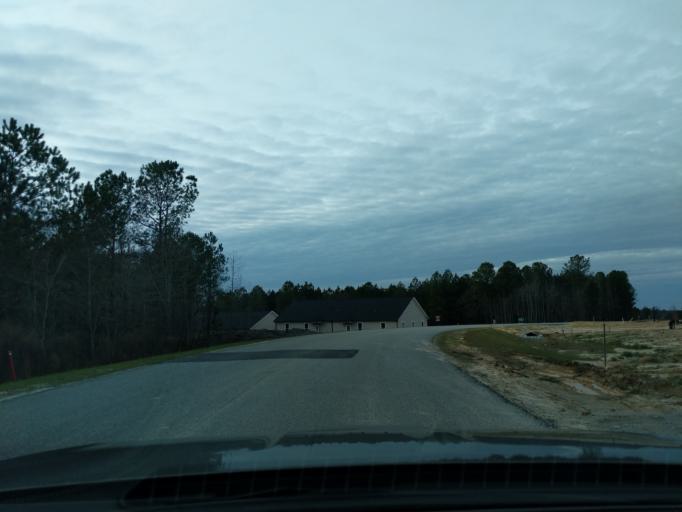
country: US
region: Georgia
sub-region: Columbia County
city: Grovetown
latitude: 33.4642
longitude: -82.1984
